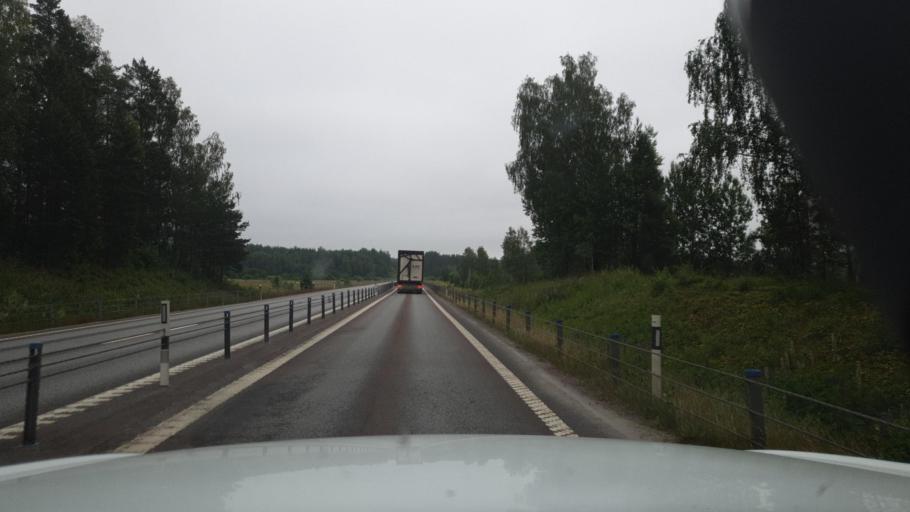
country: SE
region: Vaermland
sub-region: Arvika Kommun
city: Arvika
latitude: 59.6549
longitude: 12.6567
